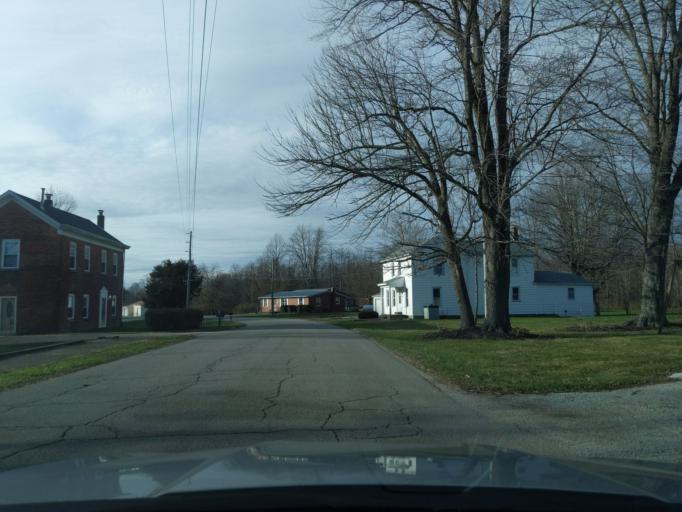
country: US
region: Indiana
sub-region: Decatur County
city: Greensburg
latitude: 39.2116
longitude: -85.4397
